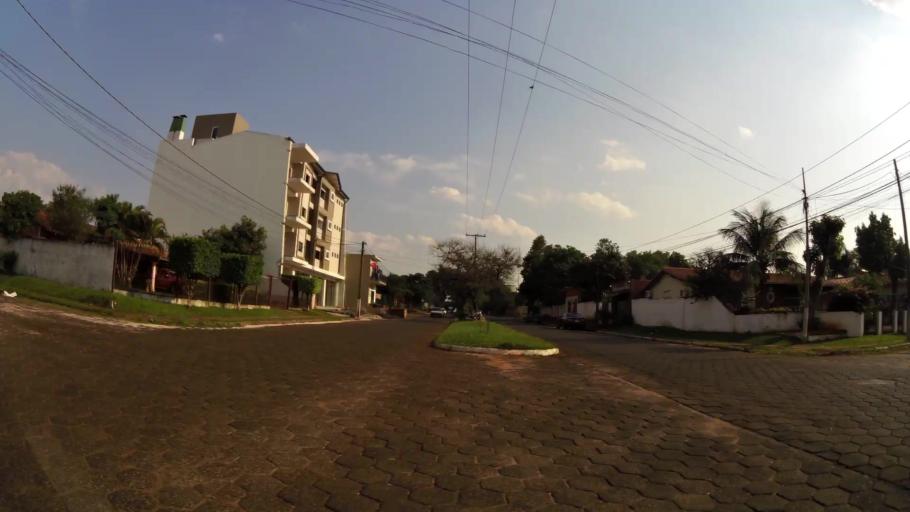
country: PY
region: Alto Parana
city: Presidente Franco
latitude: -25.5330
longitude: -54.6297
